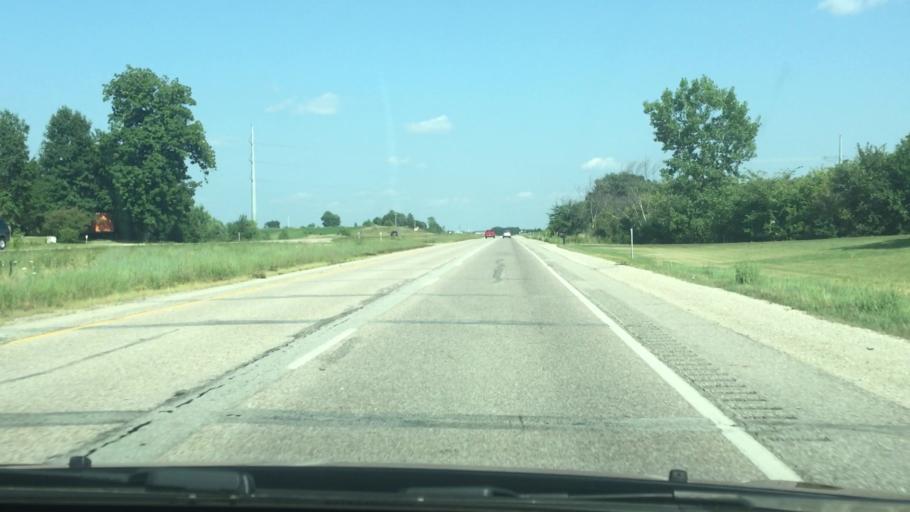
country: US
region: Iowa
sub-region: Scott County
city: Blue Grass
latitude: 41.5143
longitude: -90.8165
